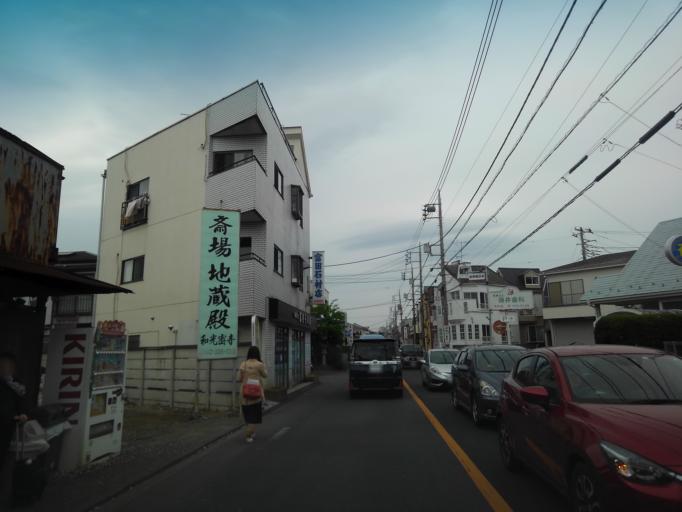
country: JP
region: Tokyo
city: Kokubunji
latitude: 35.6897
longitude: 139.5079
